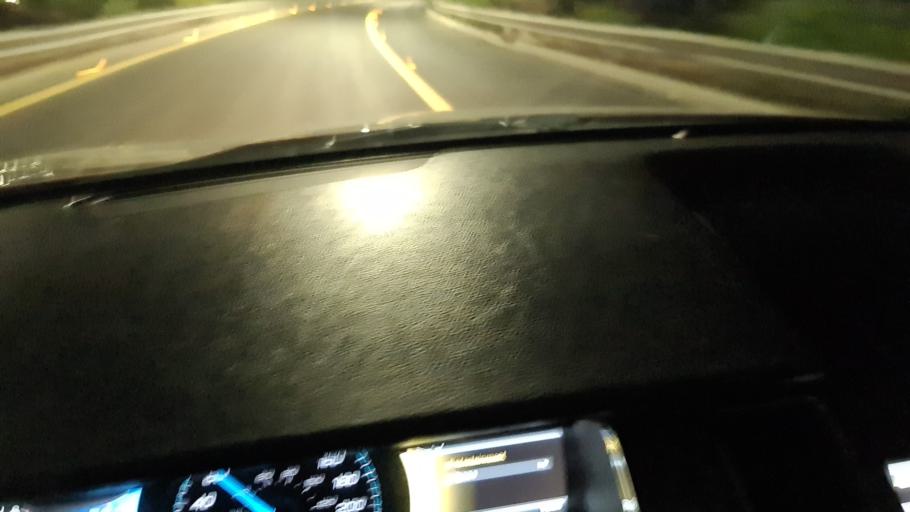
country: SA
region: Eastern Province
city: Al Jubayl
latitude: 27.1184
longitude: 49.5418
